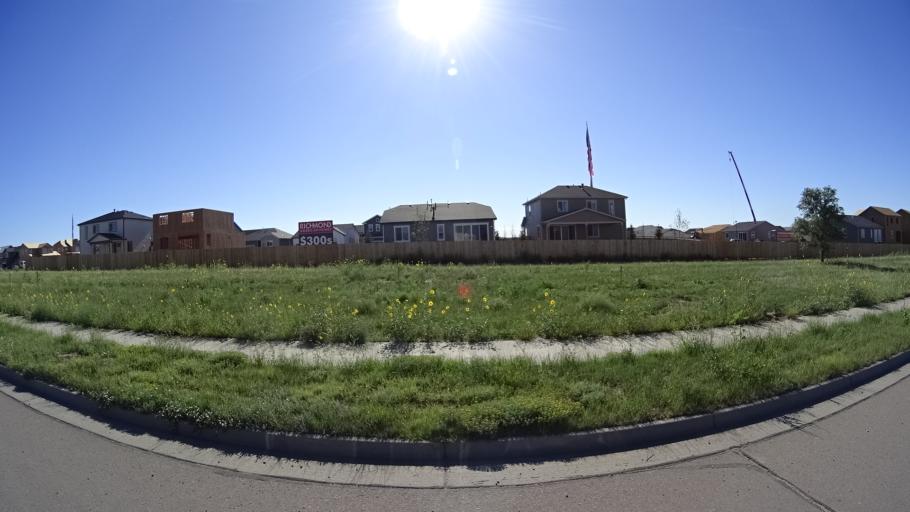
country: US
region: Colorado
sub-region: El Paso County
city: Cimarron Hills
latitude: 38.8704
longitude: -104.6827
